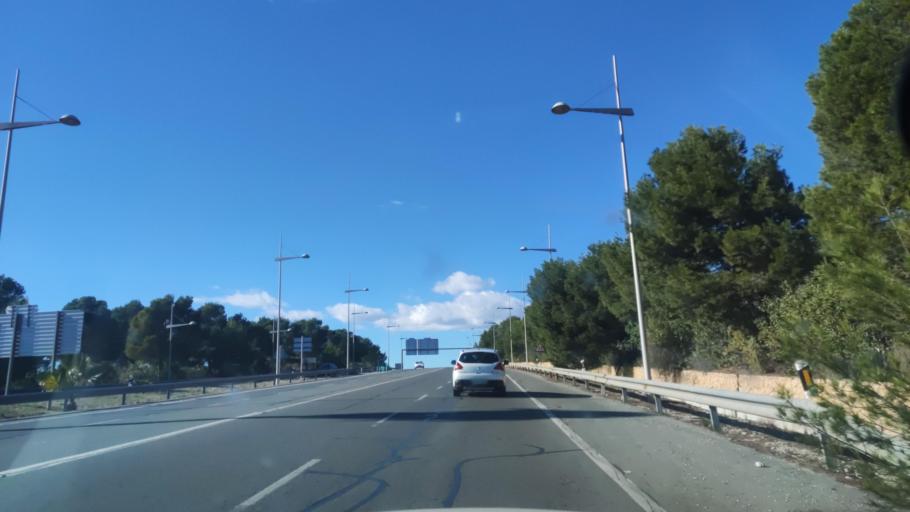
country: ES
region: Valencia
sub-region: Provincia de Alicante
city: Benidorm
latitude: 38.5494
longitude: -0.1646
